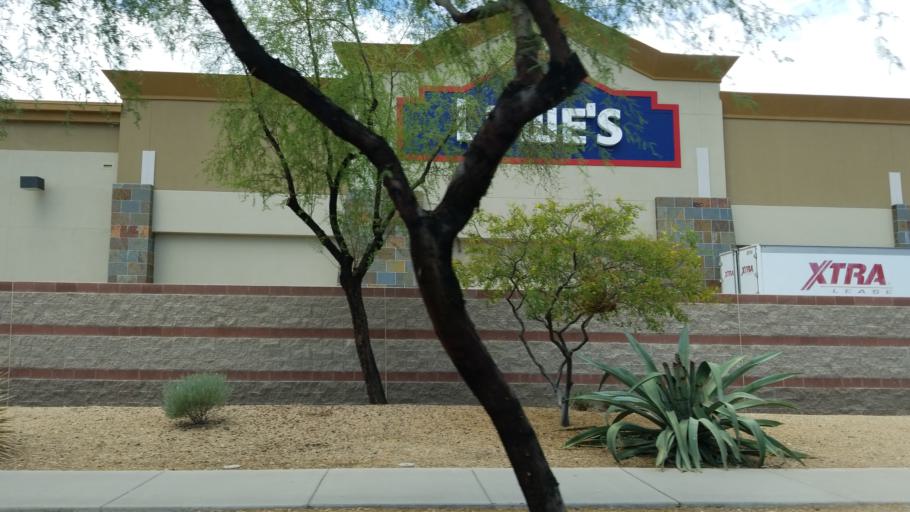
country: US
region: Arizona
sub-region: Maricopa County
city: Anthem
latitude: 33.7111
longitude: -112.1089
